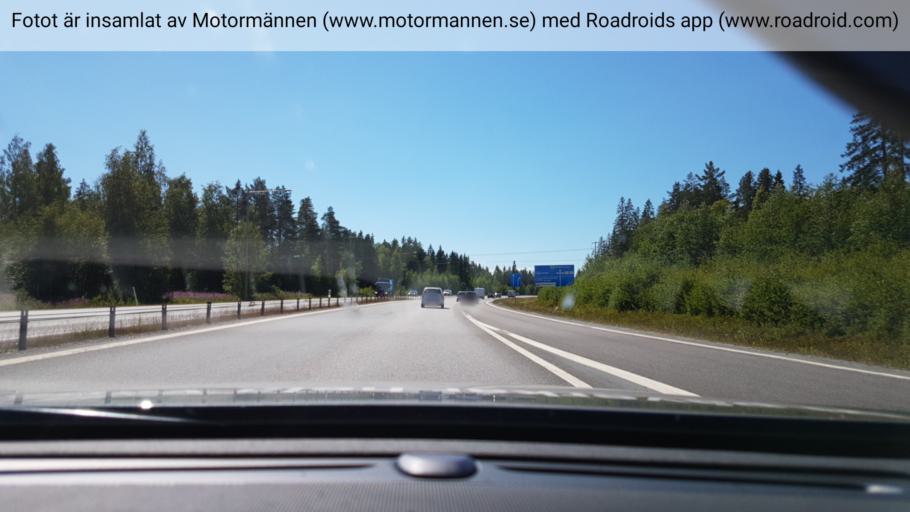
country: SE
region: Vaesterbotten
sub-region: Skelleftea Kommun
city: Skelleftea
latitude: 64.7655
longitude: 21.0141
